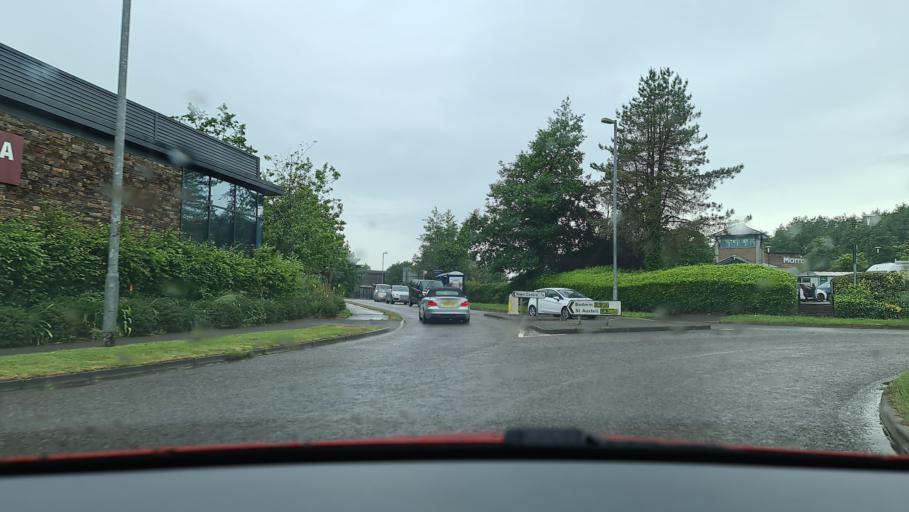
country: GB
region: England
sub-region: Cornwall
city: Liskeard
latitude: 50.4505
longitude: -4.4510
